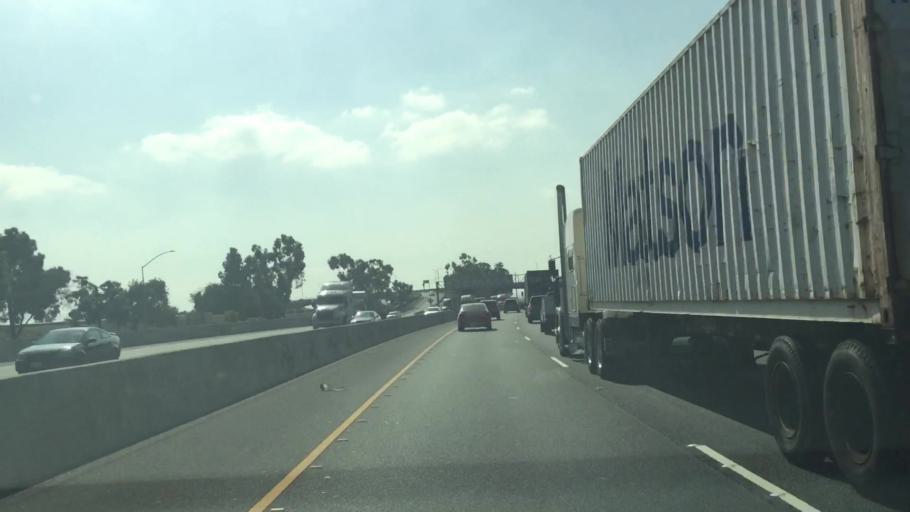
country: US
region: California
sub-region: Los Angeles County
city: Signal Hill
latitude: 33.8246
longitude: -118.2071
